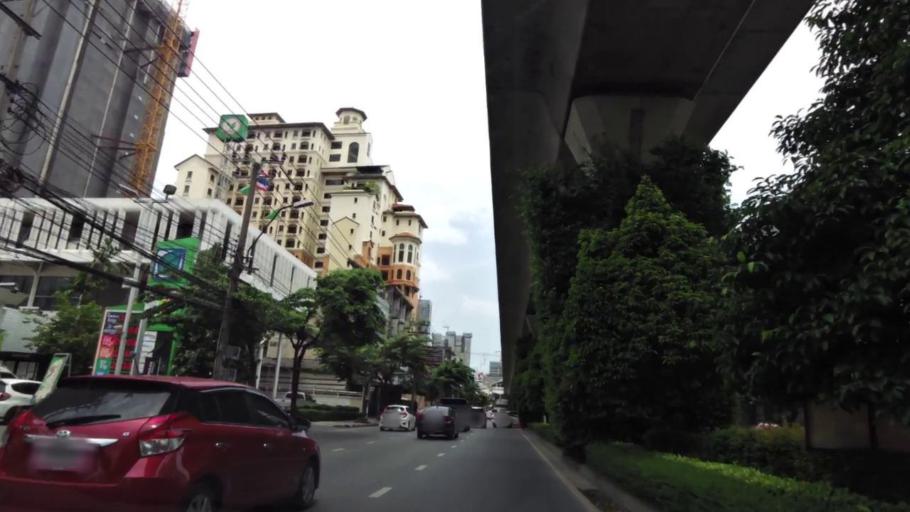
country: TH
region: Bangkok
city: Phra Khanong
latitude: 13.6926
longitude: 100.6074
